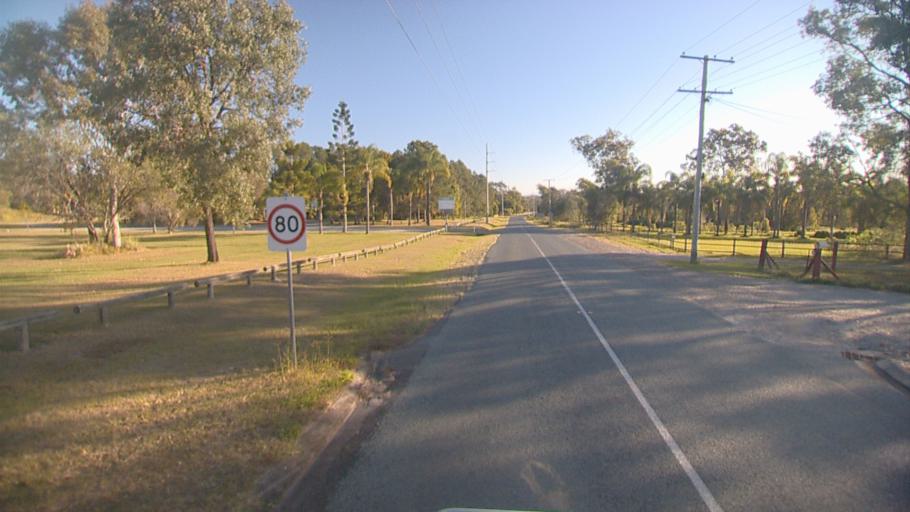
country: AU
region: Queensland
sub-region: Logan
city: Logan Reserve
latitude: -27.7249
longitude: 153.1037
